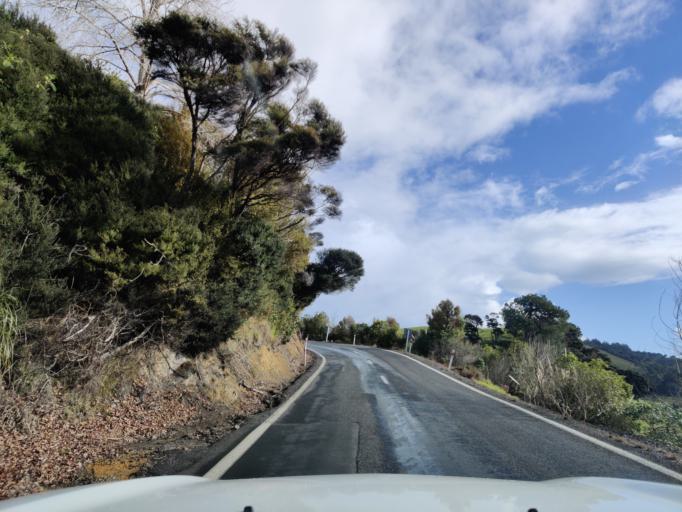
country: NZ
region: Waikato
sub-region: Thames-Coromandel District
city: Coromandel
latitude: -36.8077
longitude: 175.4948
